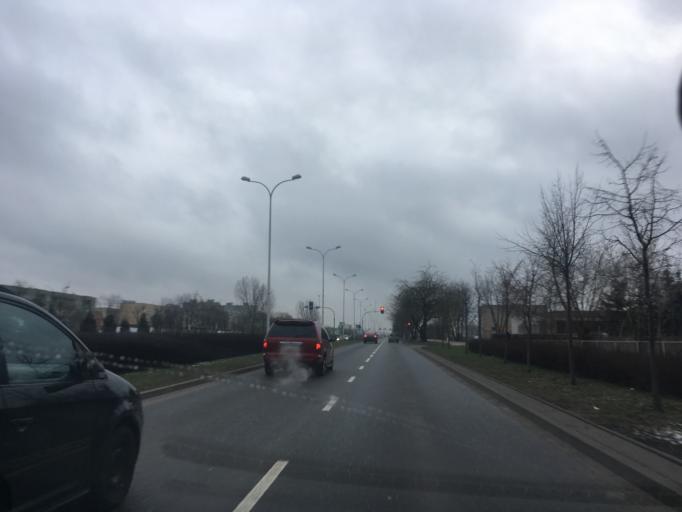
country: PL
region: Podlasie
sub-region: Suwalki
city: Suwalki
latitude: 54.1223
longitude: 22.9293
